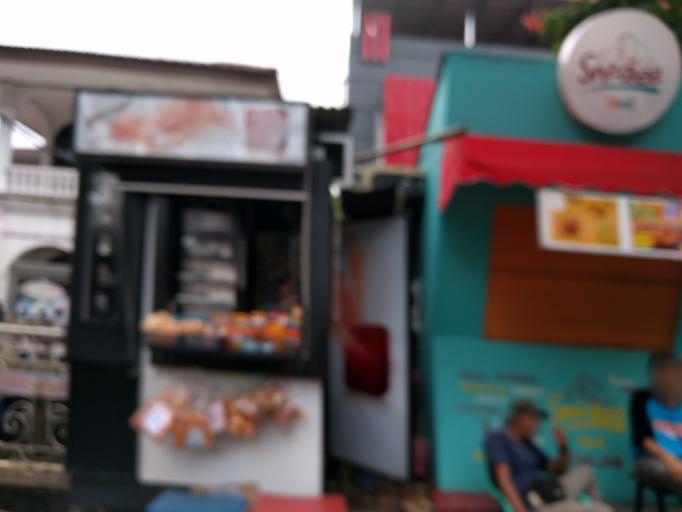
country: ID
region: West Java
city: Bogor
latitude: -6.5918
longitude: 106.8058
